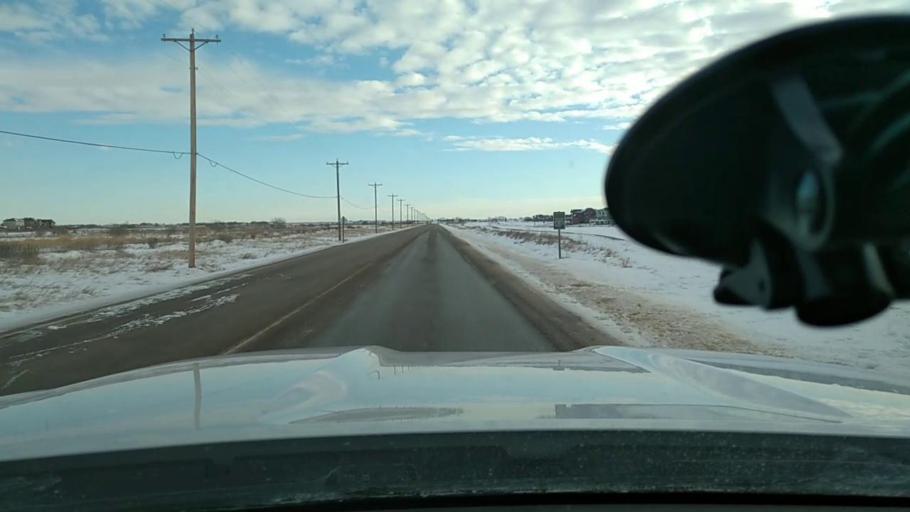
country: CA
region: Alberta
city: Chestermere
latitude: 50.9651
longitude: -113.6778
